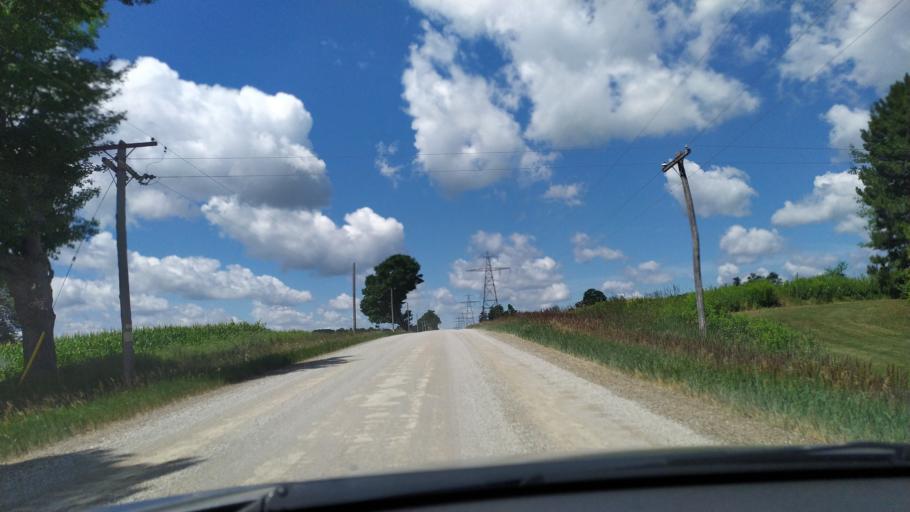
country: CA
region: Ontario
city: Stratford
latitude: 43.3875
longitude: -80.7822
